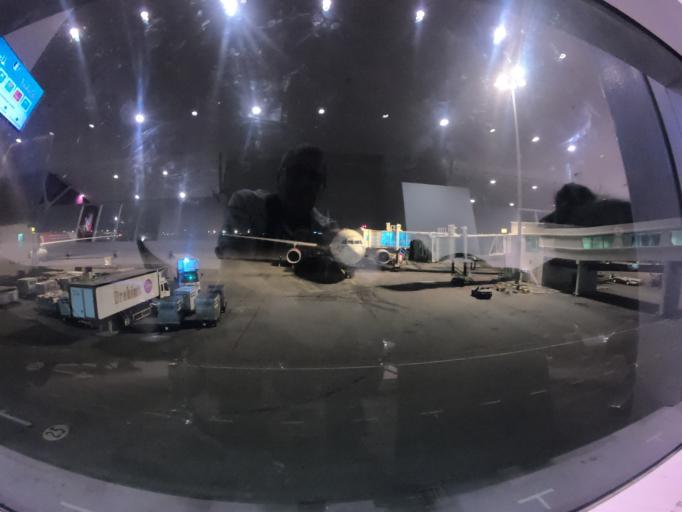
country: MY
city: Sungai Pelek New Village
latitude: 2.7407
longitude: 101.6909
